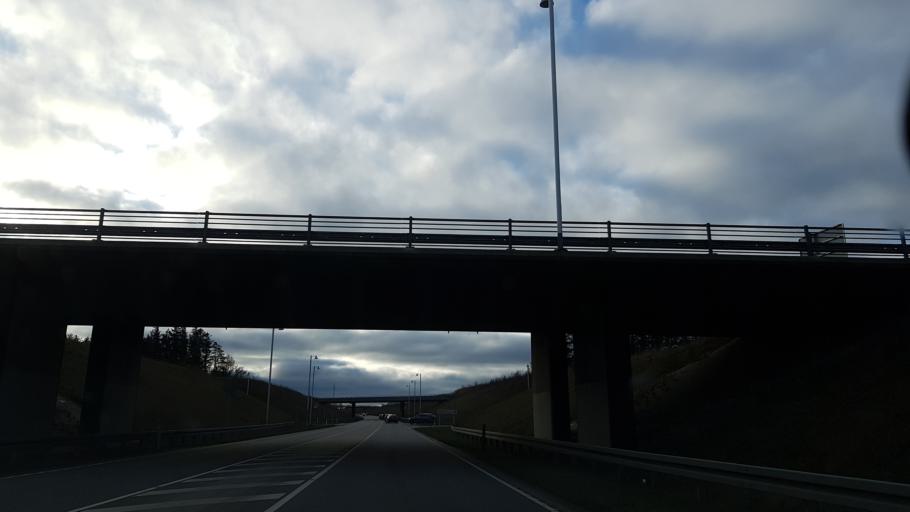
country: DK
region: Zealand
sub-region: Slagelse Kommune
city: Slagelse
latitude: 55.4153
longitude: 11.3256
